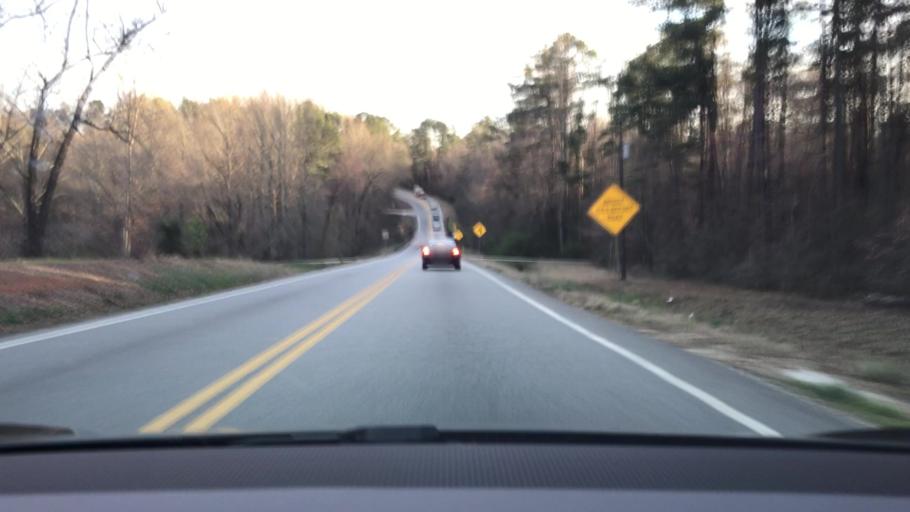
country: US
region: Georgia
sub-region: Barrow County
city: Russell
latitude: 33.9021
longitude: -83.7232
